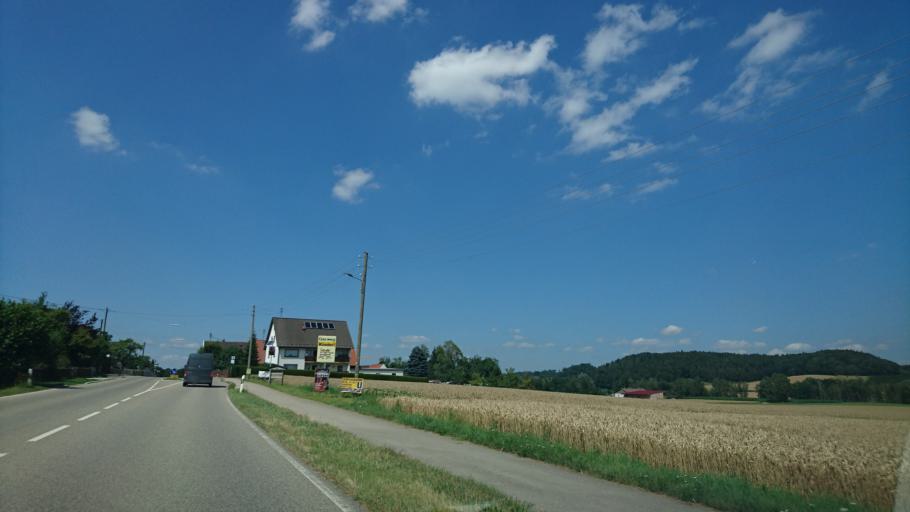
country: DE
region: Bavaria
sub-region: Swabia
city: Altenmunster
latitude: 48.4443
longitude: 10.5888
